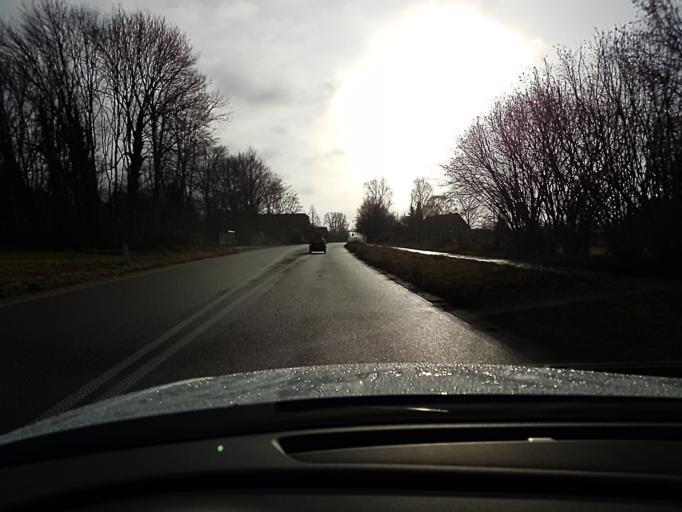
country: DE
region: North Rhine-Westphalia
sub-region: Regierungsbezirk Dusseldorf
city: Muelheim (Ruhr)
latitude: 51.3991
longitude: 6.9006
